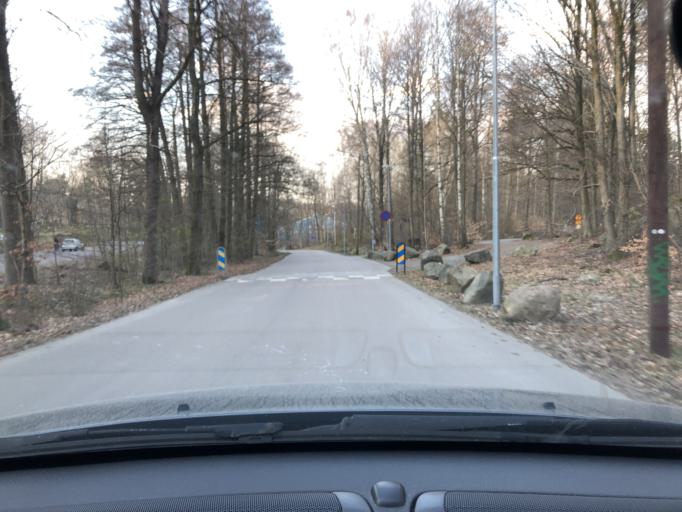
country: SE
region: Vaestra Goetaland
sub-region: Molndal
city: Moelndal
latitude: 57.6923
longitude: 12.0344
